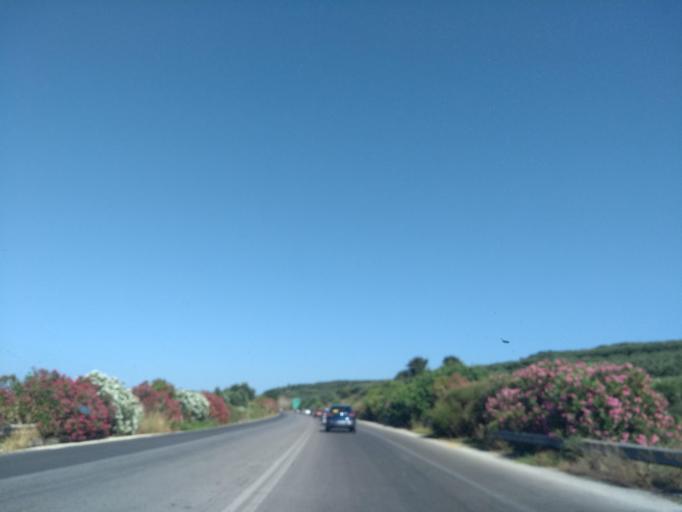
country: GR
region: Crete
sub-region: Nomos Chanias
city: Kolympari
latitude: 35.5252
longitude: 23.8019
